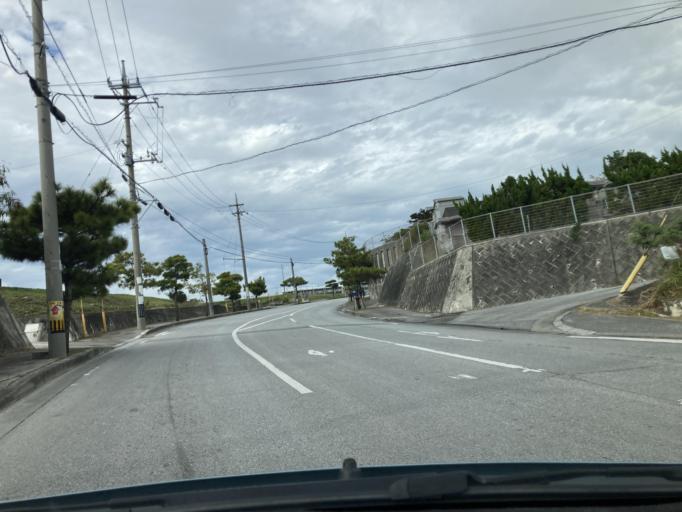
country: JP
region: Okinawa
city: Naha-shi
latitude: 26.2138
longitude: 127.7302
